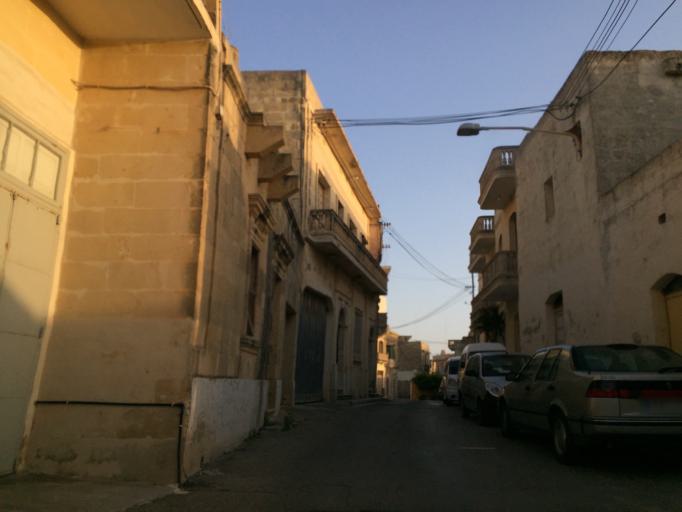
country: MT
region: Ix-Xaghra
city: Xaghra
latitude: 36.0485
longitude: 14.2633
